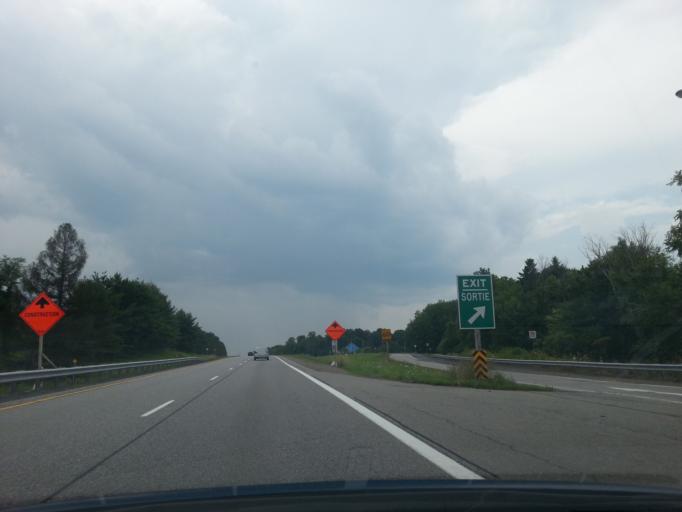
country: CA
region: Quebec
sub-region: Monteregie
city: Rigaud
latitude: 45.5466
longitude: -74.4181
